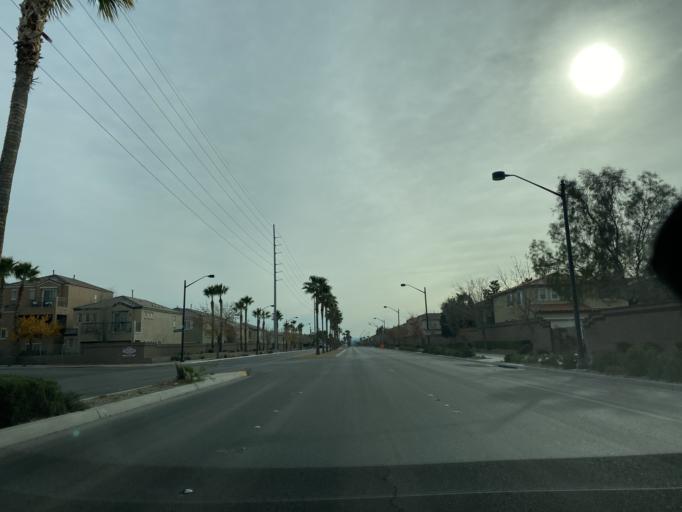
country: US
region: Nevada
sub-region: Clark County
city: Summerlin South
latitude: 36.2977
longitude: -115.2969
